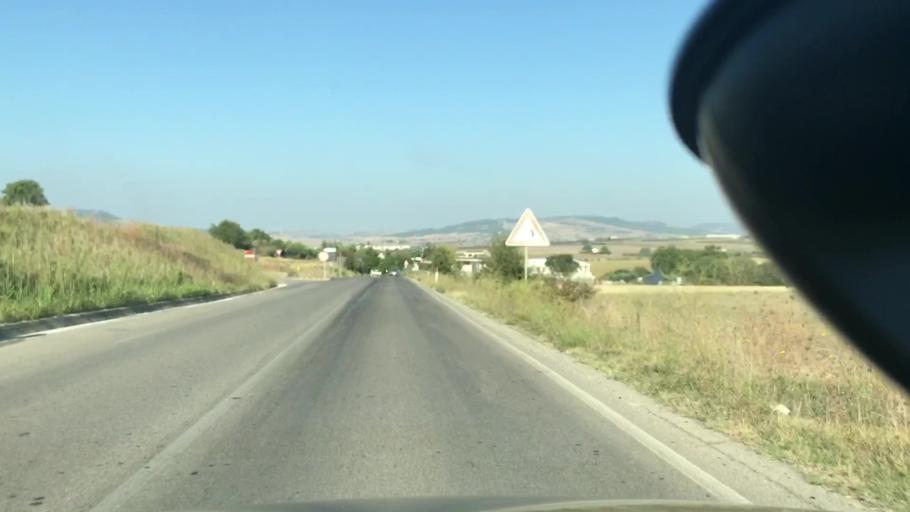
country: IT
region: Basilicate
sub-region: Provincia di Matera
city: La Martella
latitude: 40.6601
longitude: 16.5662
